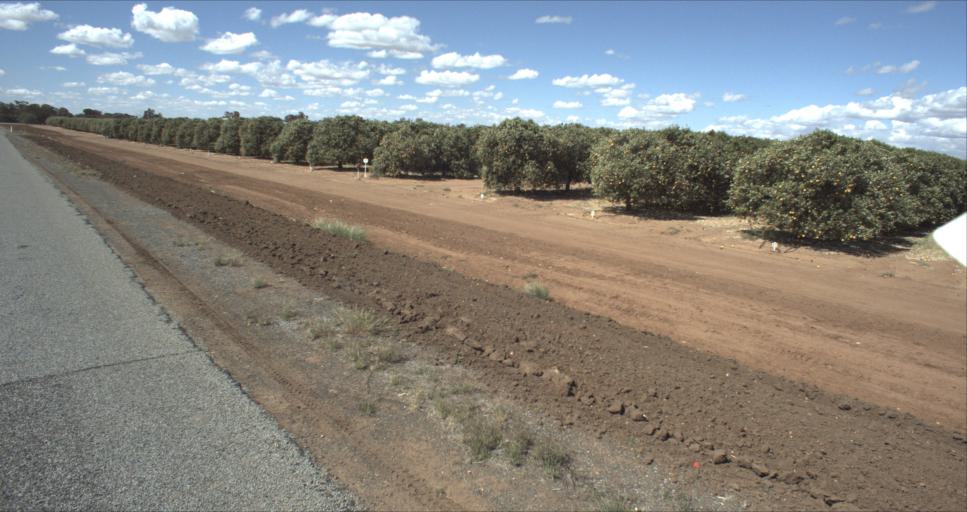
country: AU
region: New South Wales
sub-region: Leeton
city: Leeton
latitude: -34.5209
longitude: 146.2240
